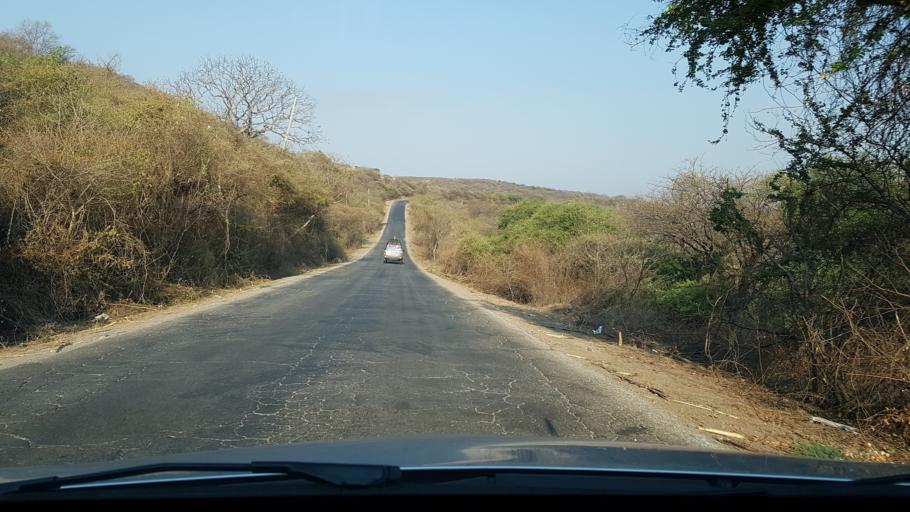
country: MX
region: Morelos
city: Tlaltizapan
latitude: 18.6761
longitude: -99.0727
